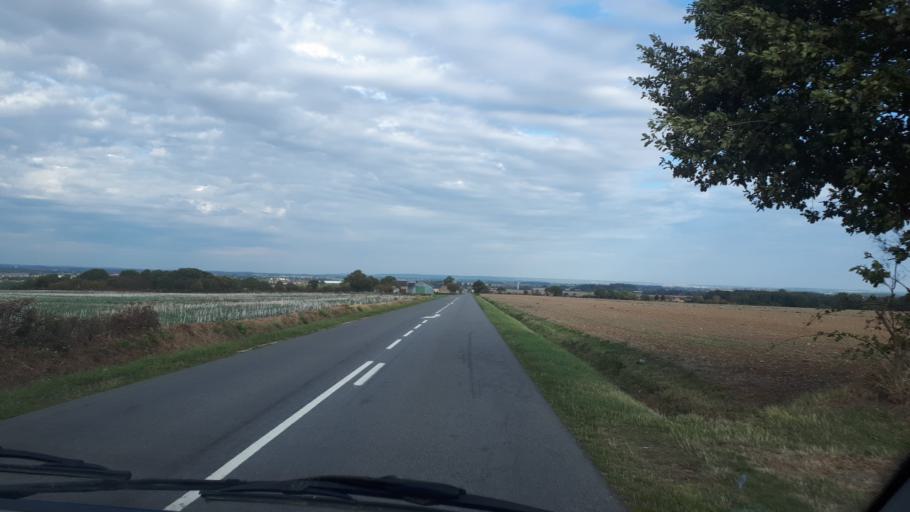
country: FR
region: Centre
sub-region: Departement du Loir-et-Cher
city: Mondoubleau
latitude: 47.9594
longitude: 0.9304
